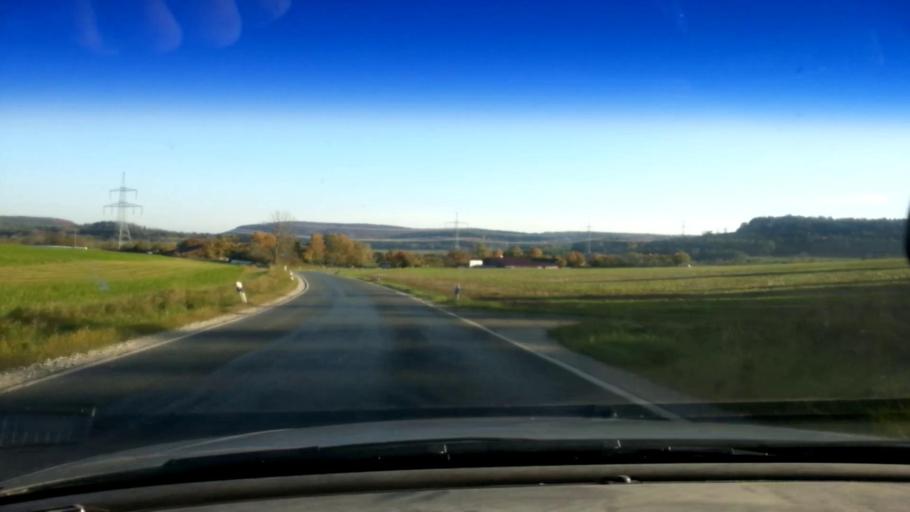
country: DE
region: Bavaria
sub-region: Upper Franconia
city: Poxdorf
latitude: 49.8951
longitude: 11.1005
